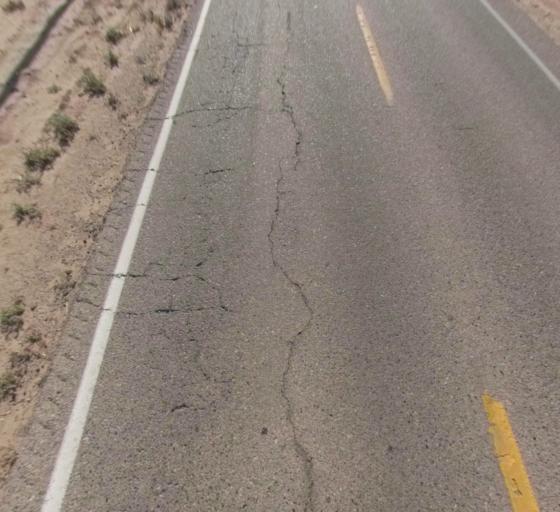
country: US
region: California
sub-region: Fresno County
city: Biola
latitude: 36.8513
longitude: -119.9635
